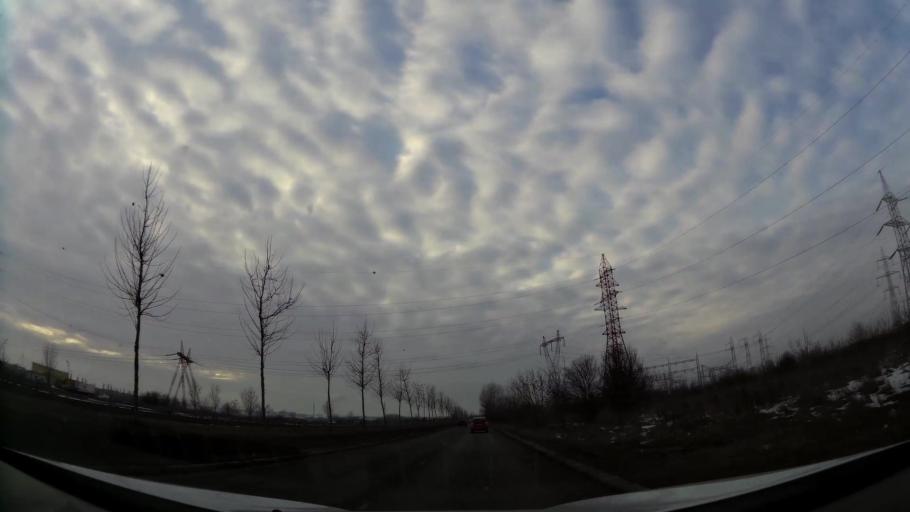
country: RO
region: Ilfov
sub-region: Comuna Popesti-Leordeni
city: Popesti-Leordeni
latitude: 44.3945
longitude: 26.1854
